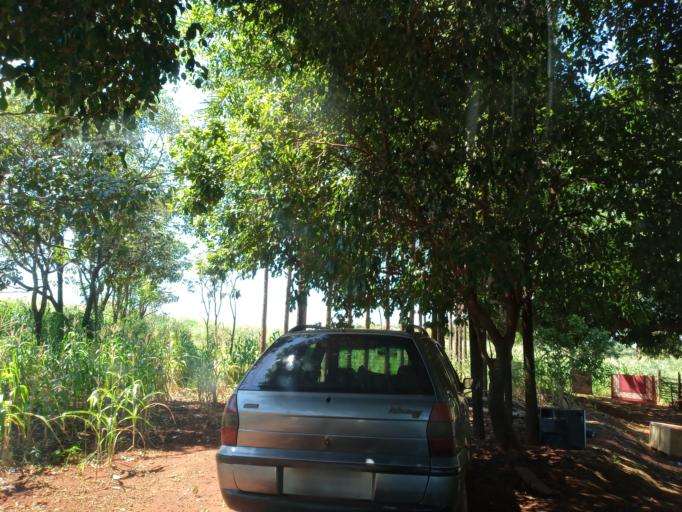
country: BR
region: Goias
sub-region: Itumbiara
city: Itumbiara
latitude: -18.4410
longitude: -49.1318
